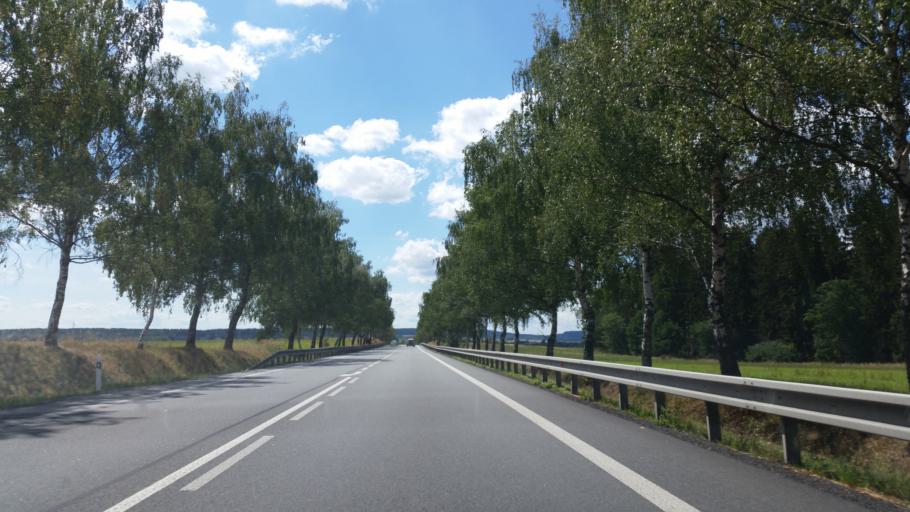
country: CZ
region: Vysocina
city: Nova Cerekev
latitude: 49.4277
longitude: 15.0686
